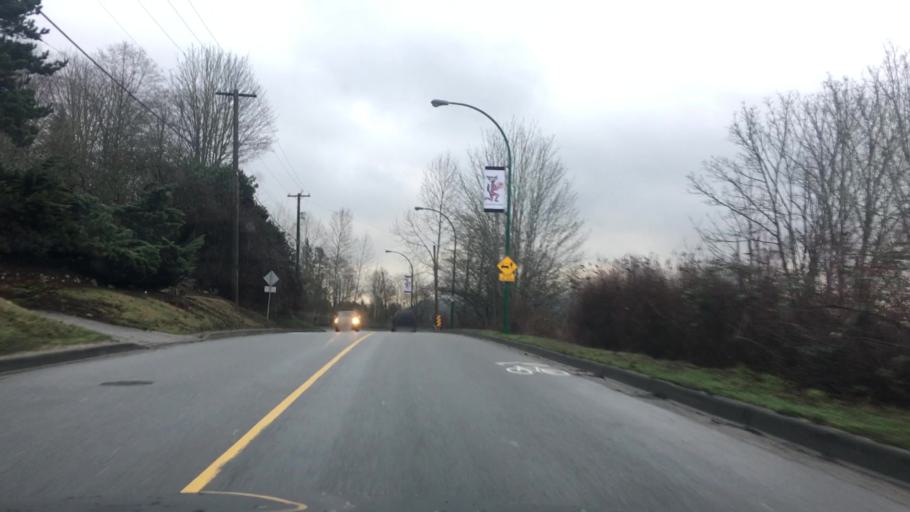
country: CA
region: British Columbia
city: Burnaby
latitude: 49.3082
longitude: -122.9845
